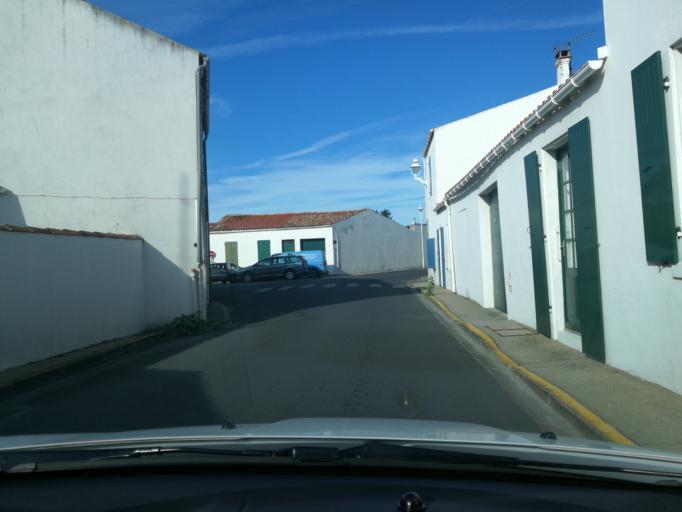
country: FR
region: Poitou-Charentes
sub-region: Departement de la Charente-Maritime
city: Saint-Denis-d'Oleron
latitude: 46.0332
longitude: -1.3814
